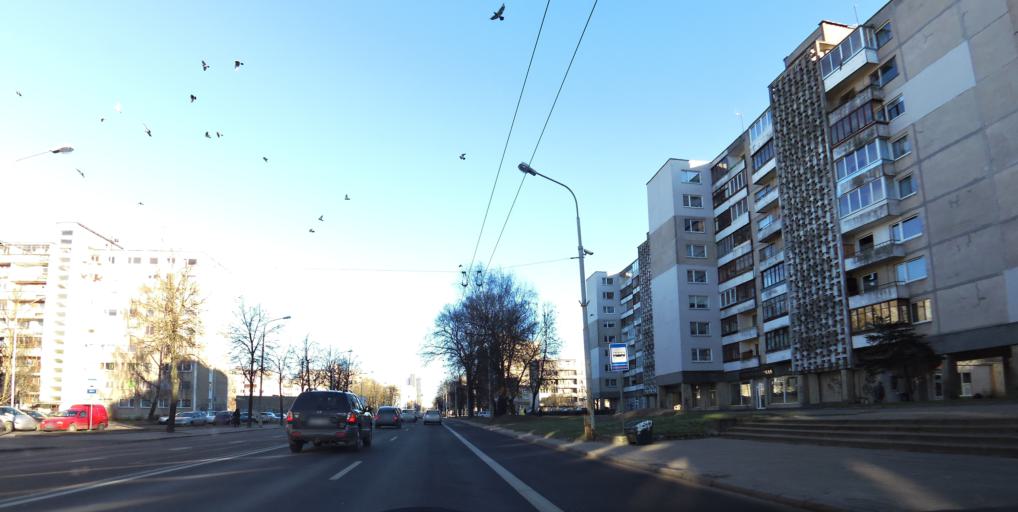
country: LT
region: Vilnius County
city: Vilkpede
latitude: 54.6718
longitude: 25.2441
